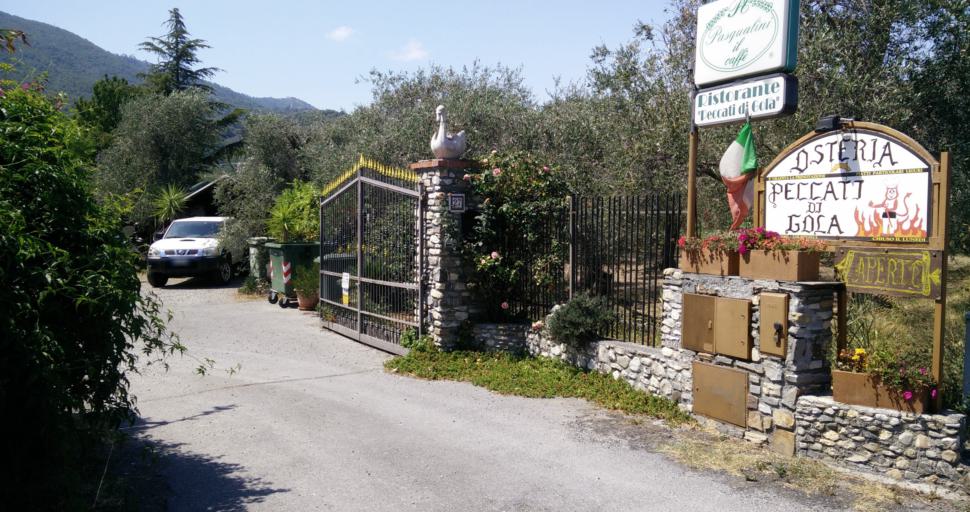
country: IT
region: Liguria
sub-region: Provincia di Savona
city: Andora
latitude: 43.9732
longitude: 8.1377
